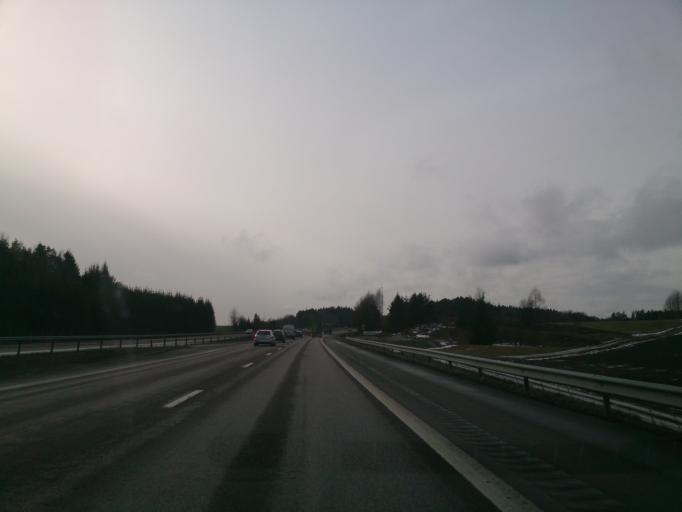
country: SE
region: Soedermanland
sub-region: Gnesta Kommun
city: Gnesta
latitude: 58.8806
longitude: 17.2434
